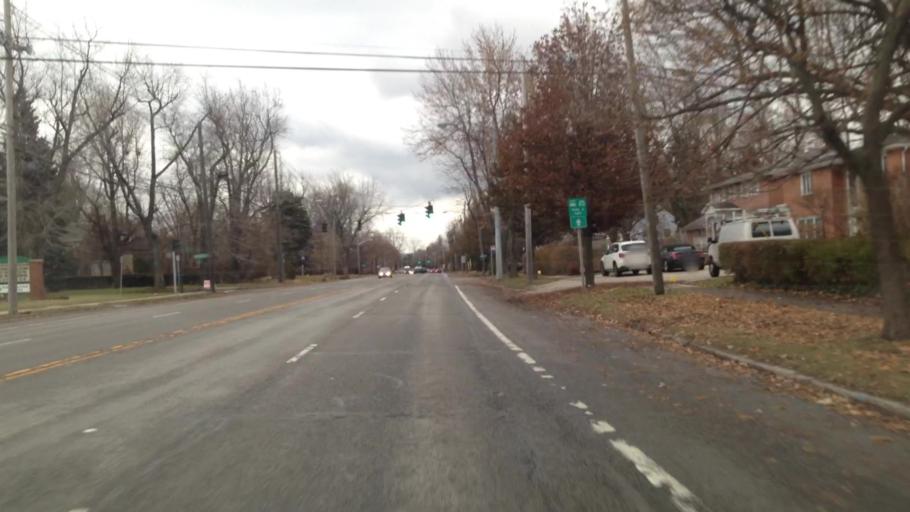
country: US
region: New York
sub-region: Erie County
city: Eggertsville
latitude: 42.9620
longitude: -78.7796
